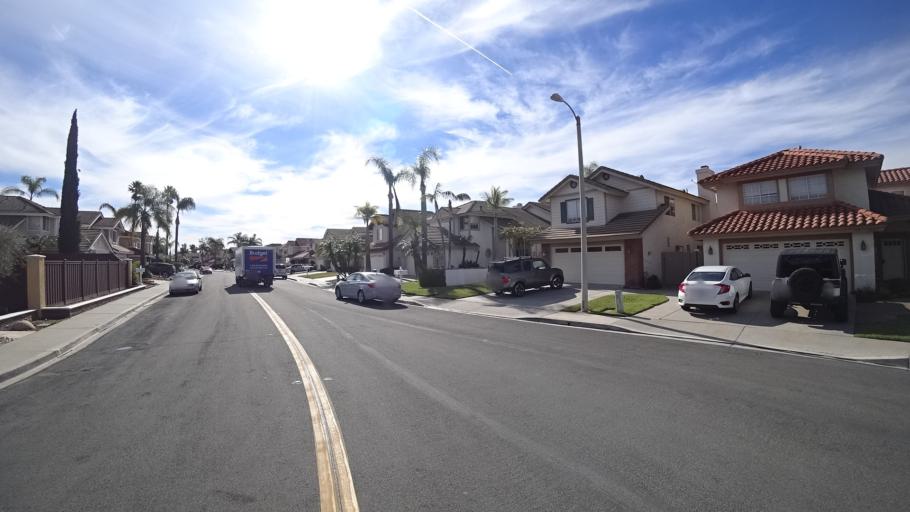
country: US
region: California
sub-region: Orange County
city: Portola Hills
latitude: 33.6892
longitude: -117.6297
